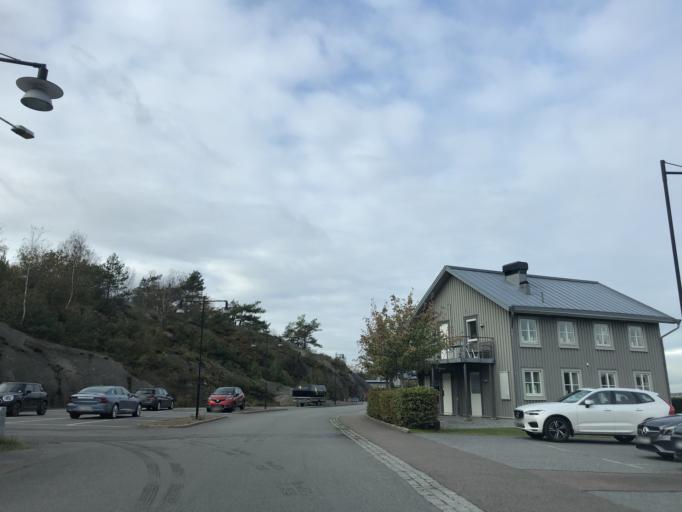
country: SE
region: Vaestra Goetaland
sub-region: Goteborg
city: Majorna
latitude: 57.6847
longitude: 11.8827
